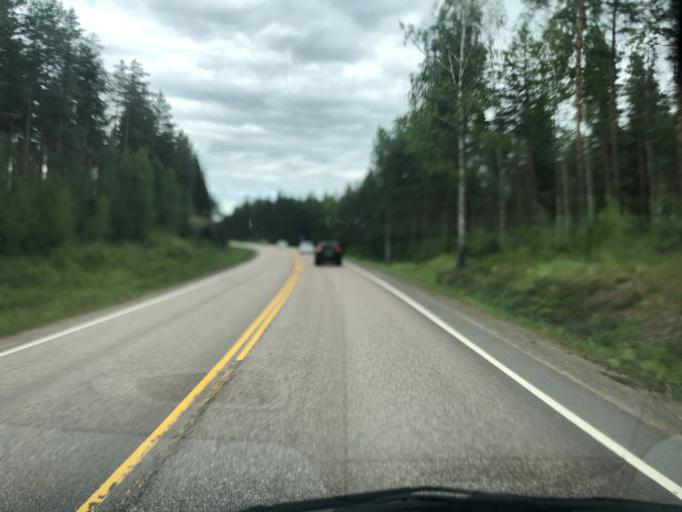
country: FI
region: Southern Savonia
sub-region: Mikkeli
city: Maentyharju
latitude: 61.1500
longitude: 27.1368
